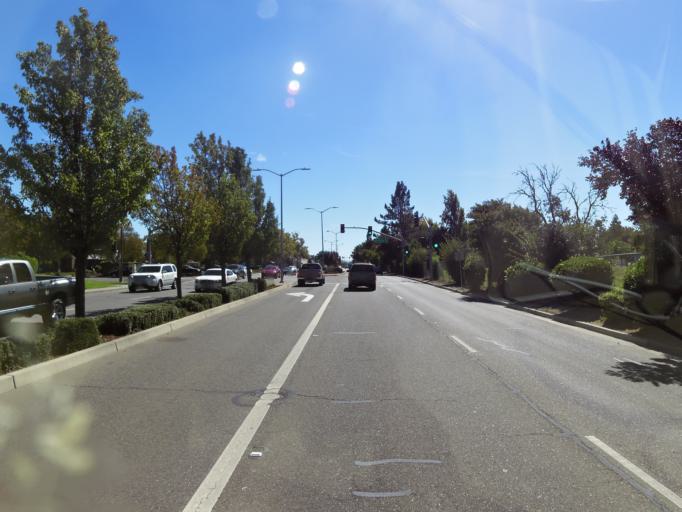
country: US
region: California
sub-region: Solano County
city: Fairfield
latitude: 38.2521
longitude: -122.0500
